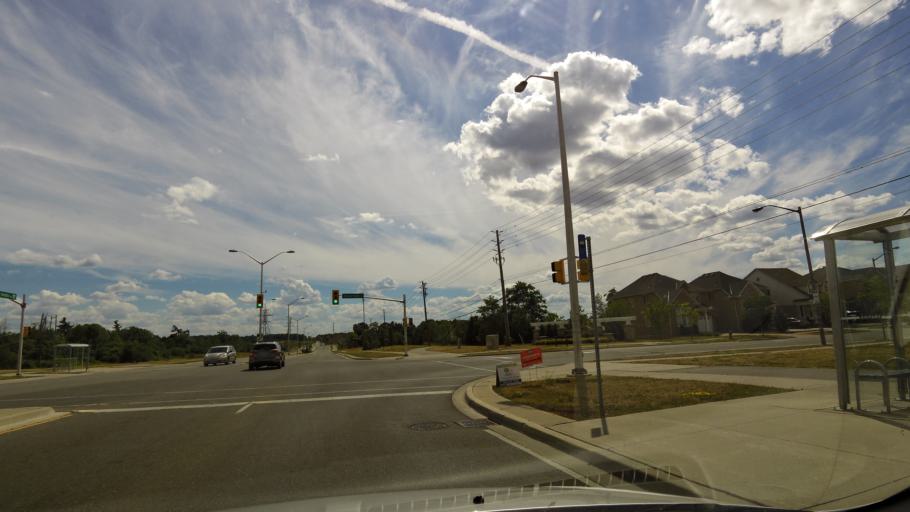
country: CA
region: Ontario
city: Oakville
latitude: 43.4270
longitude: -79.7546
